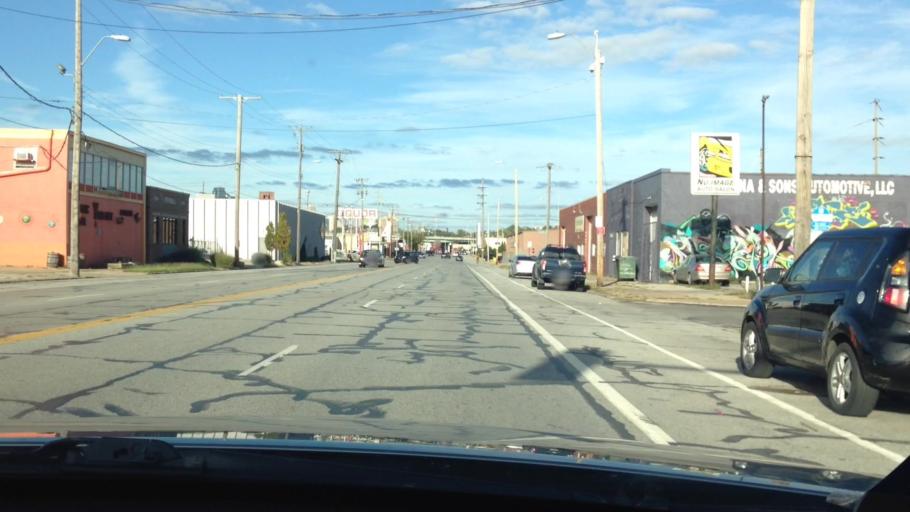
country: US
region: Kansas
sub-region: Johnson County
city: Westwood
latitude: 39.0725
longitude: -94.6072
